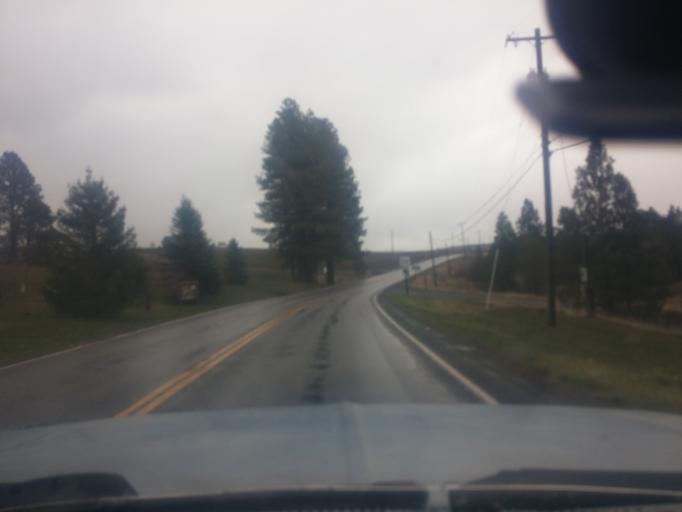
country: US
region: Idaho
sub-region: Latah County
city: Moscow
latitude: 46.9215
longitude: -116.8897
